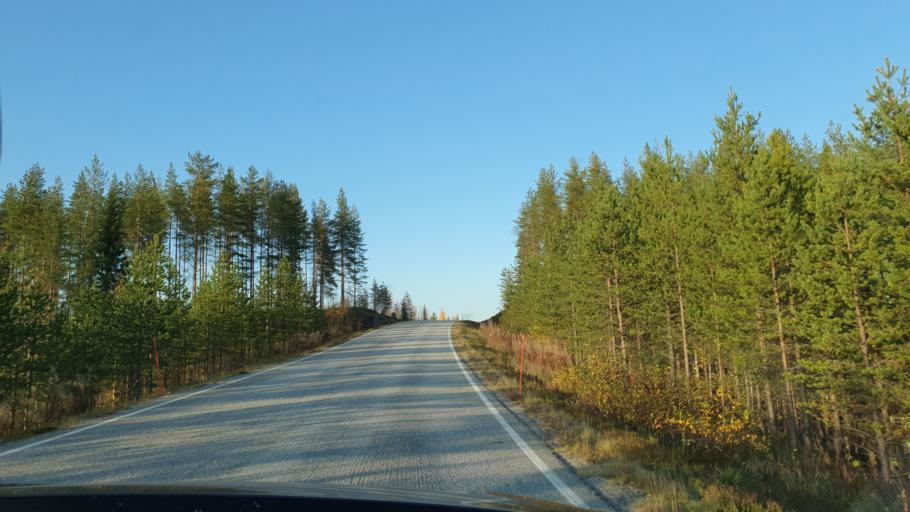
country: FI
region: Kainuu
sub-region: Kehys-Kainuu
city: Kuhmo
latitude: 64.3652
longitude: 29.4888
